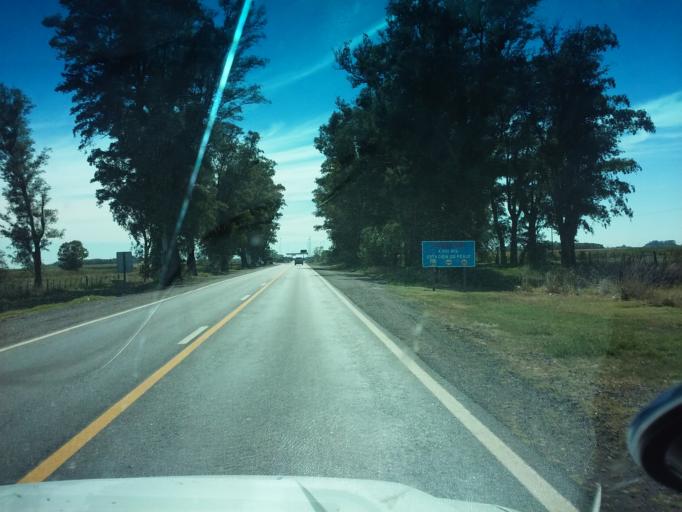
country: AR
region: Buenos Aires
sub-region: Partido de Nueve de Julio
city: Nueve de Julio
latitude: -35.3639
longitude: -60.7069
